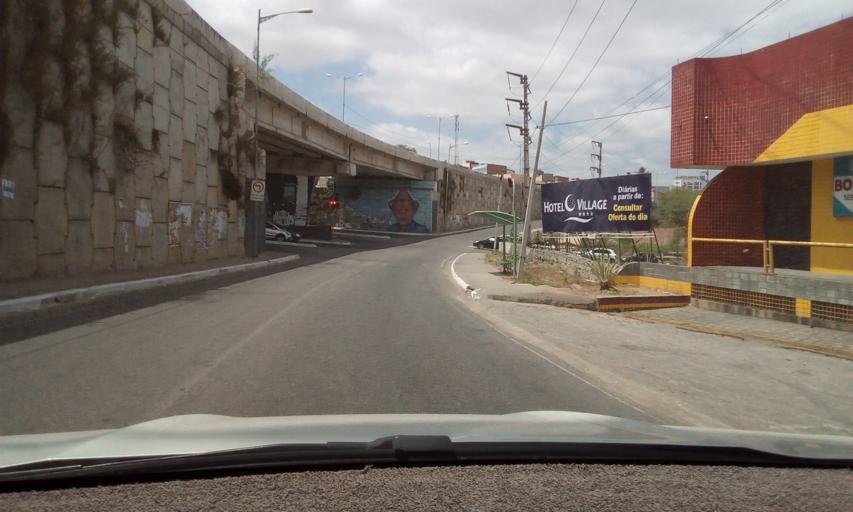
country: BR
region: Pernambuco
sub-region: Caruaru
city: Caruaru
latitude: -8.2816
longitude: -35.9814
